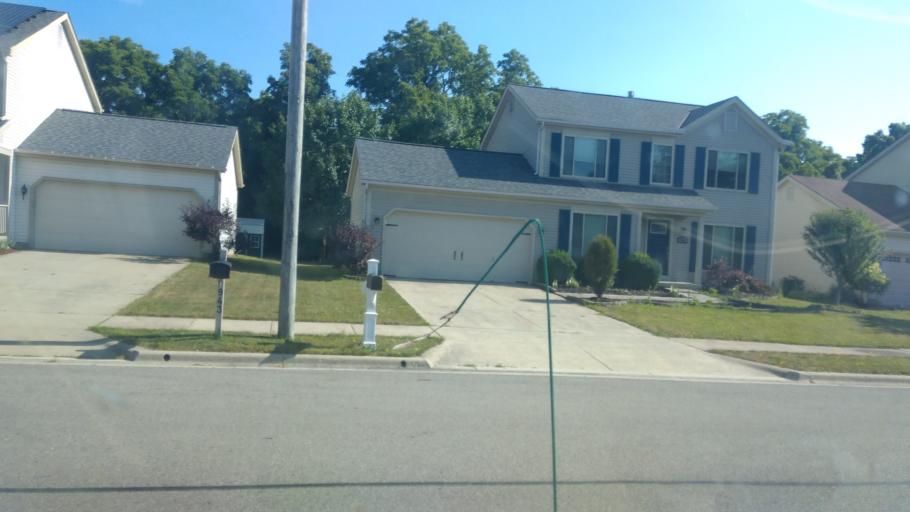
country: US
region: Ohio
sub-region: Delaware County
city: Delaware
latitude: 40.3245
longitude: -83.0799
